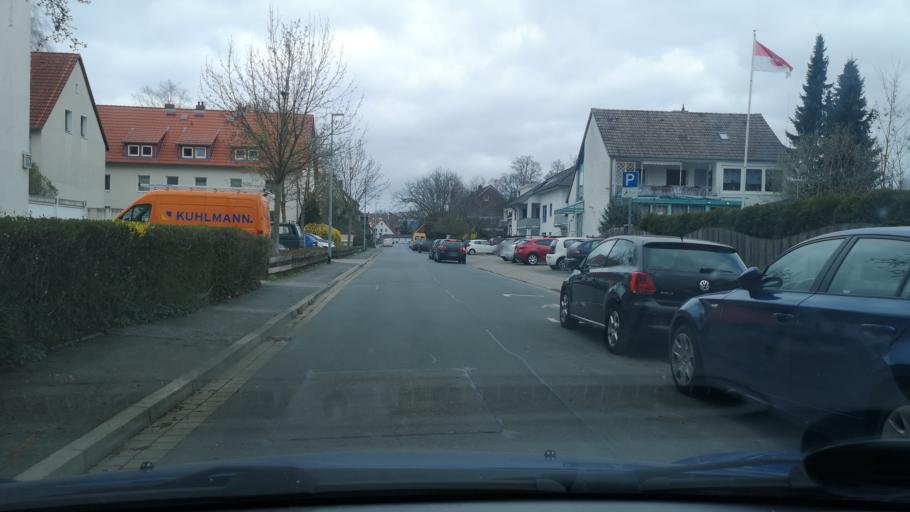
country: DE
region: Lower Saxony
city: Langenhagen
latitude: 52.4349
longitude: 9.7094
